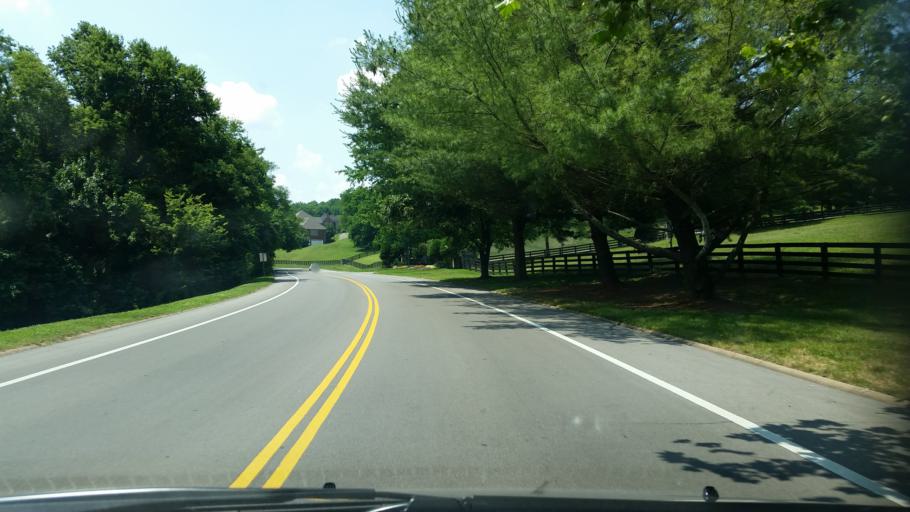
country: US
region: Tennessee
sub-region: Williamson County
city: Brentwood Estates
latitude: 35.9890
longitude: -86.7519
